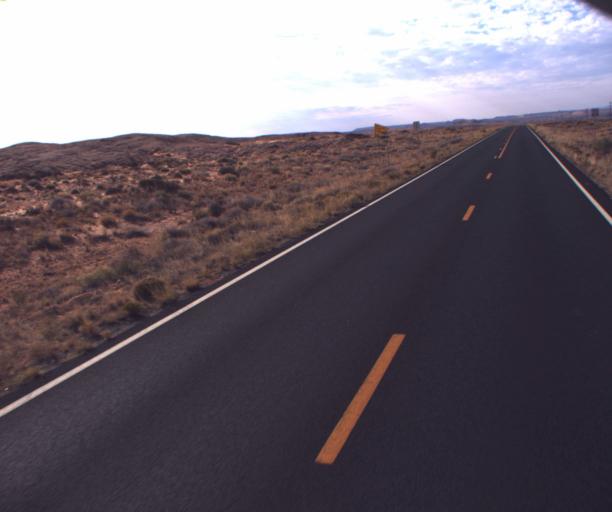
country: US
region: Arizona
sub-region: Apache County
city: Many Farms
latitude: 36.8280
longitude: -109.6441
